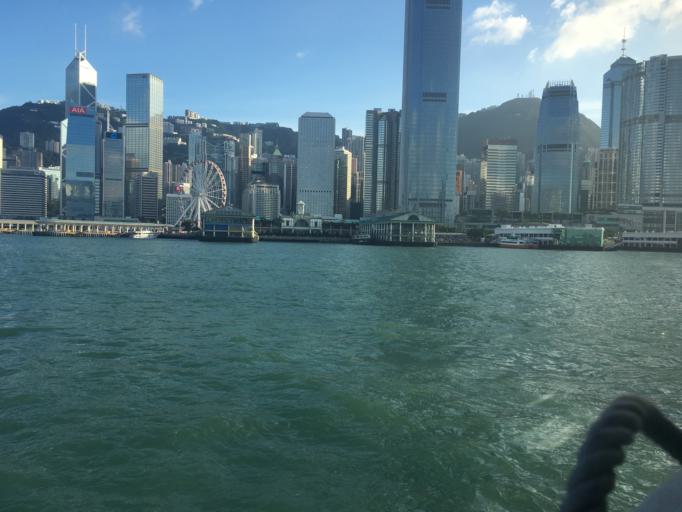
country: HK
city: Hong Kong
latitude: 22.2896
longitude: 114.1634
